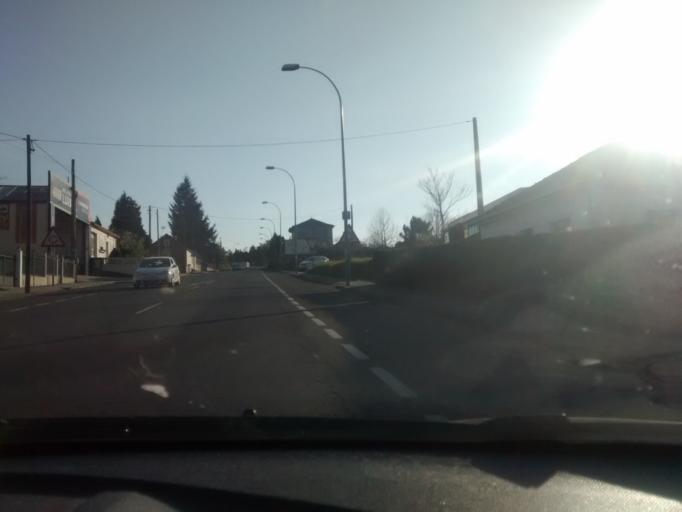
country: ES
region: Galicia
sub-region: Provincia de Pontevedra
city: A Estrada
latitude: 42.6919
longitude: -8.4696
